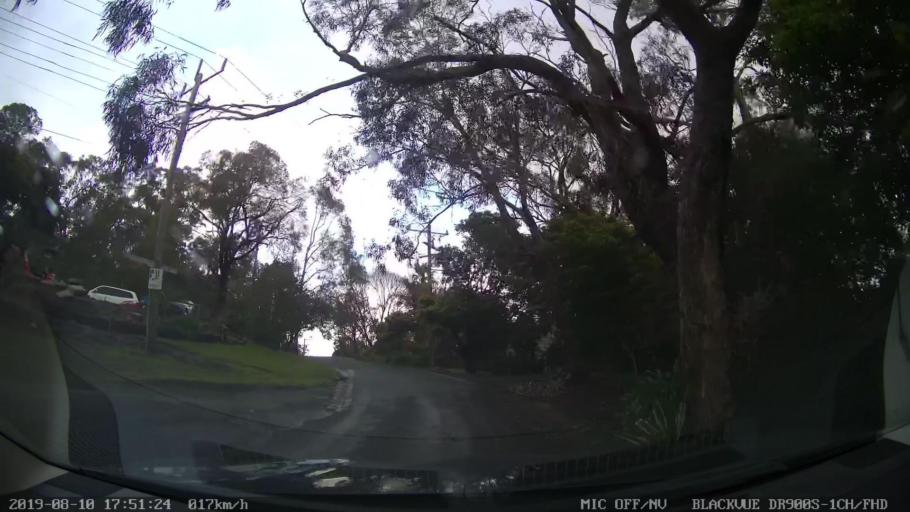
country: AU
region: Victoria
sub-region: Yarra Ranges
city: Tremont
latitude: -37.8970
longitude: 145.3247
